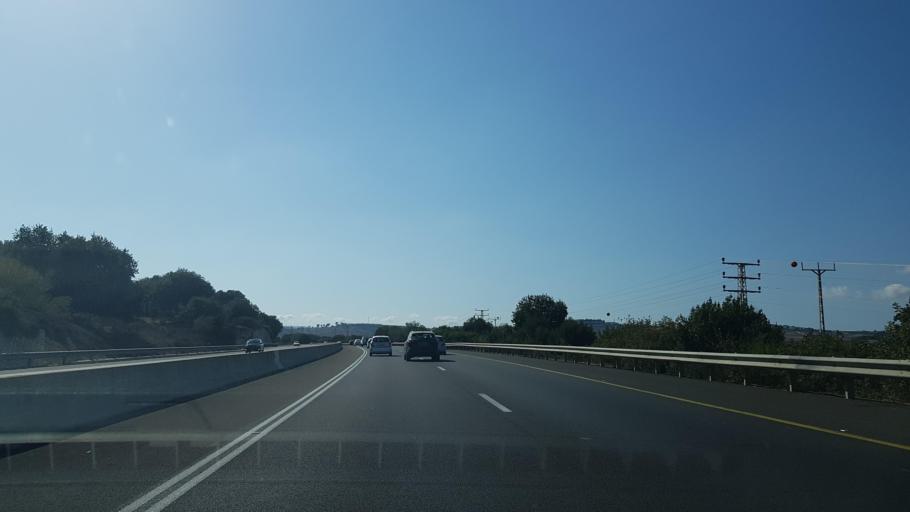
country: IL
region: Northern District
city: Kafr Manda
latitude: 32.7719
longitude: 35.2589
